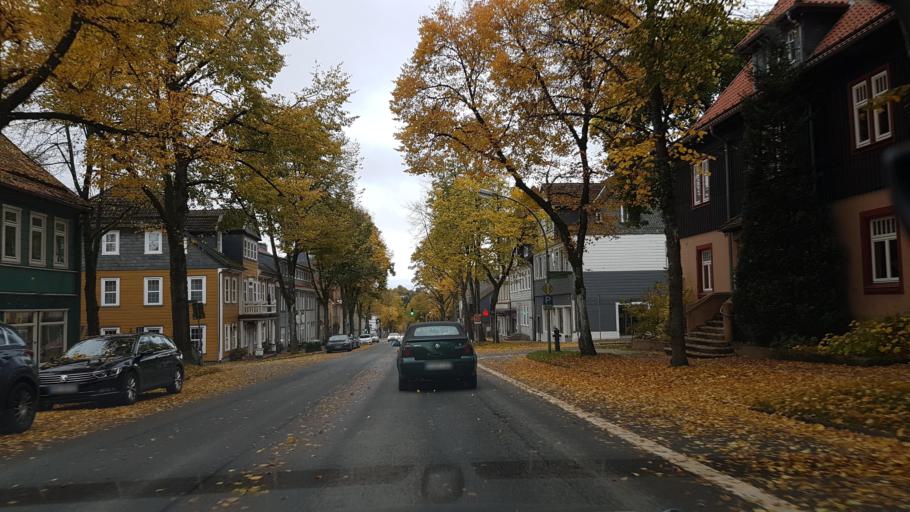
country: DE
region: Lower Saxony
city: Clausthal-Zellerfeld
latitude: 51.8179
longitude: 10.3377
